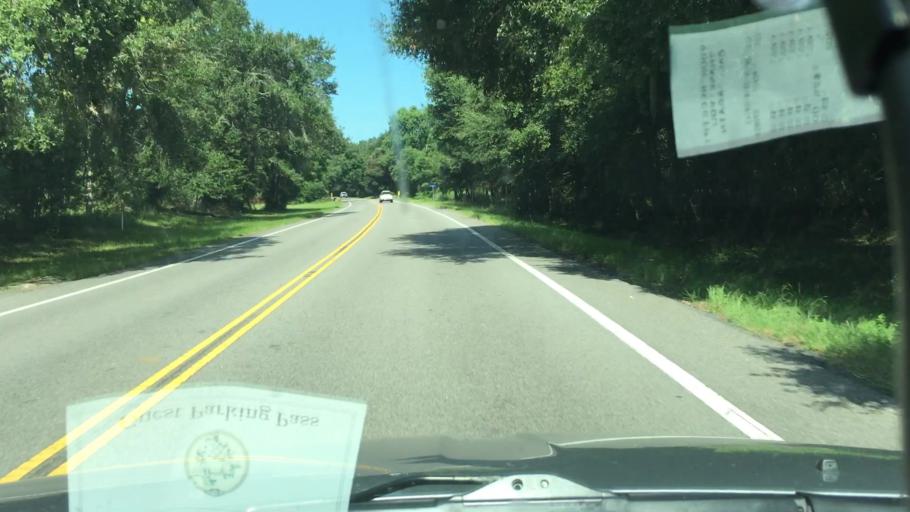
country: US
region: South Carolina
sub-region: Beaufort County
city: Beaufort
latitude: 32.4150
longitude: -80.4849
